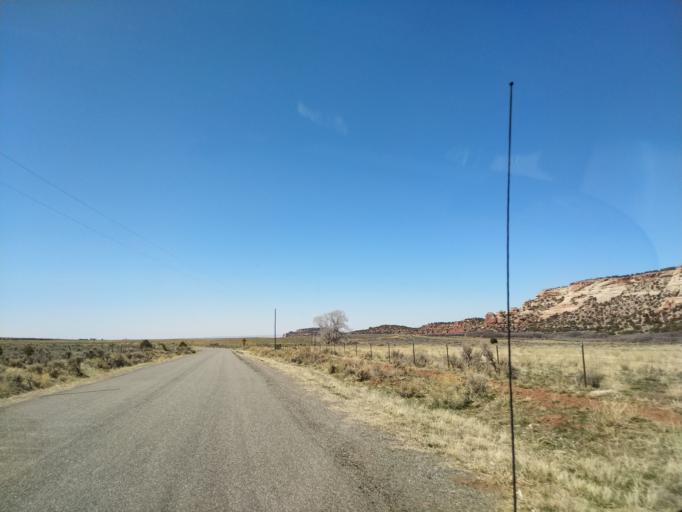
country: US
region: Colorado
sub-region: Mesa County
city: Loma
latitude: 38.9541
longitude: -109.0285
